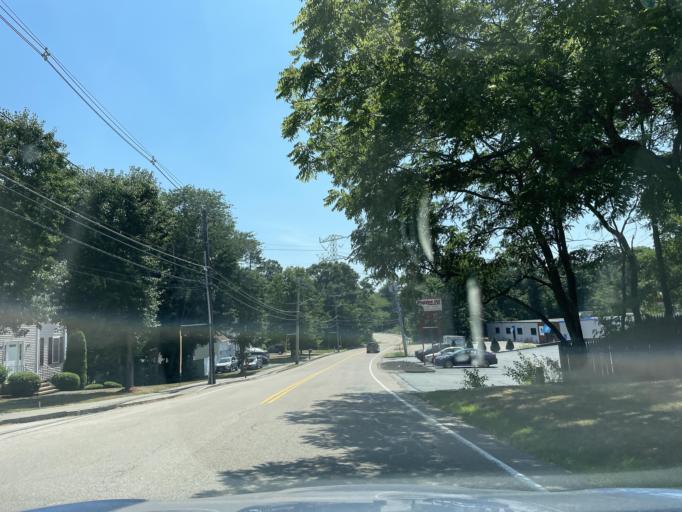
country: US
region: Massachusetts
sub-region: Norfolk County
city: Randolph
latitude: 42.1601
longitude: -71.0247
